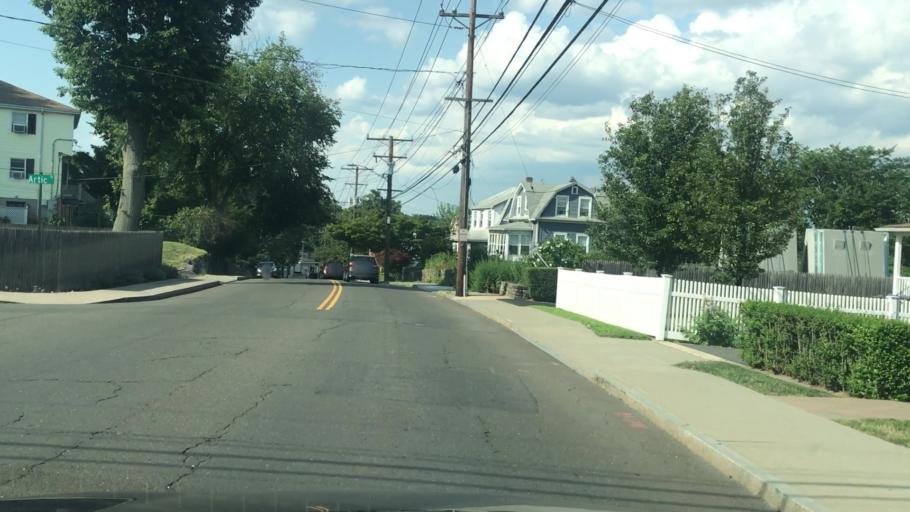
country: US
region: Connecticut
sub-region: Fairfield County
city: Greenwich
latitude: 41.0193
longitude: -73.6383
